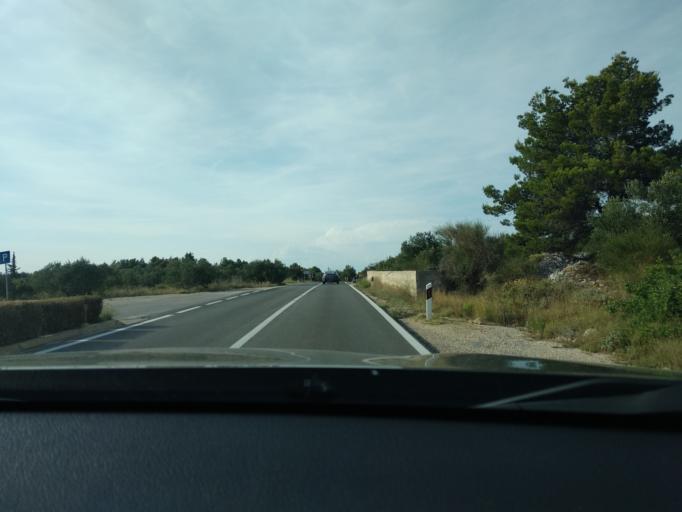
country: HR
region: Sibensko-Kniniska
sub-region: Grad Sibenik
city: Tisno
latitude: 43.7928
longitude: 15.6327
